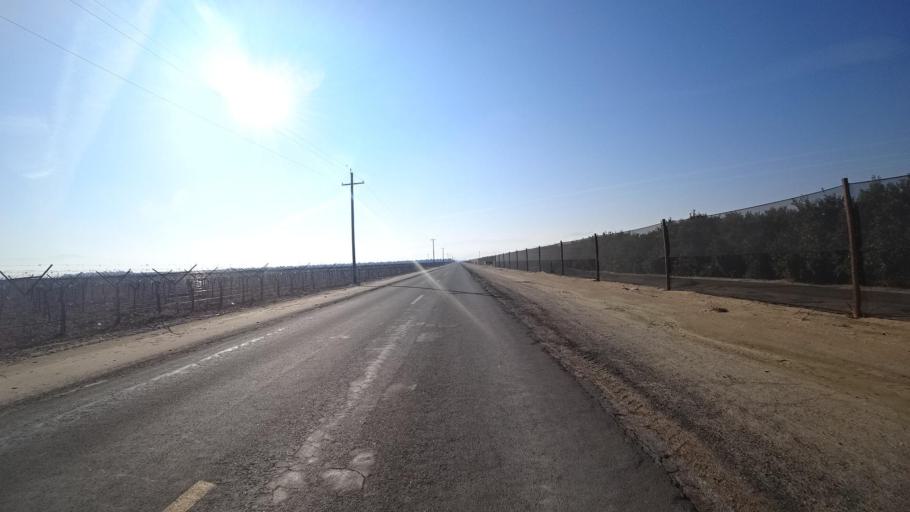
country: US
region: California
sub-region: Kern County
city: Weedpatch
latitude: 35.1183
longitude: -118.9676
